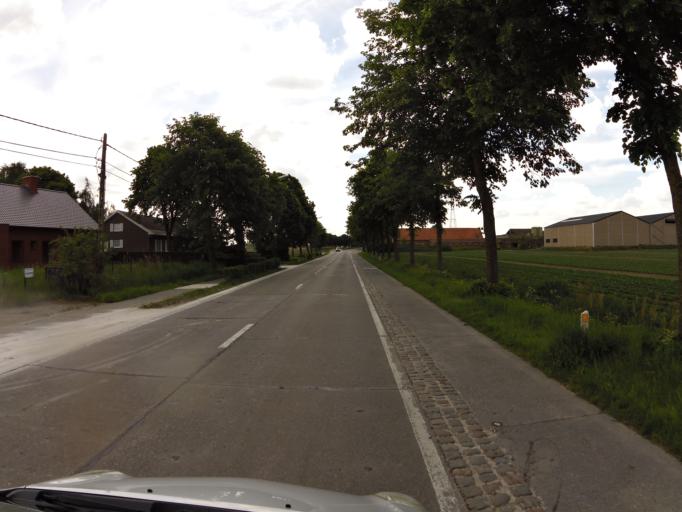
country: BE
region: Flanders
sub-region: Provincie West-Vlaanderen
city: Ieper
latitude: 50.8820
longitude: 2.9284
